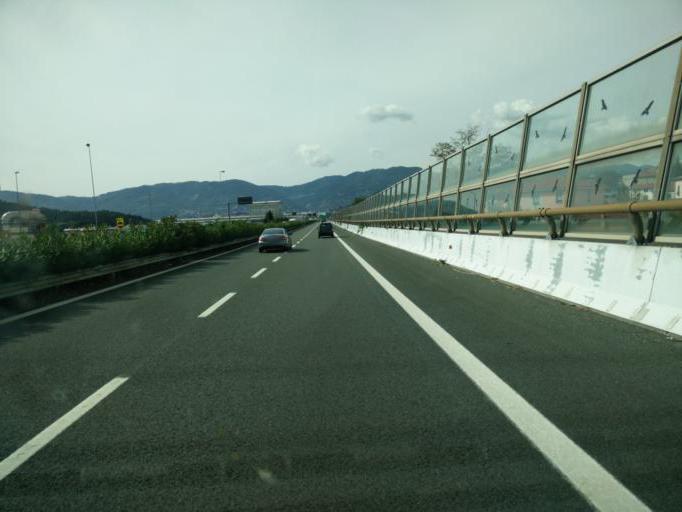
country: IT
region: Liguria
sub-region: Provincia di La Spezia
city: Stazione-Fornola
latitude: 44.1161
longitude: 9.8794
